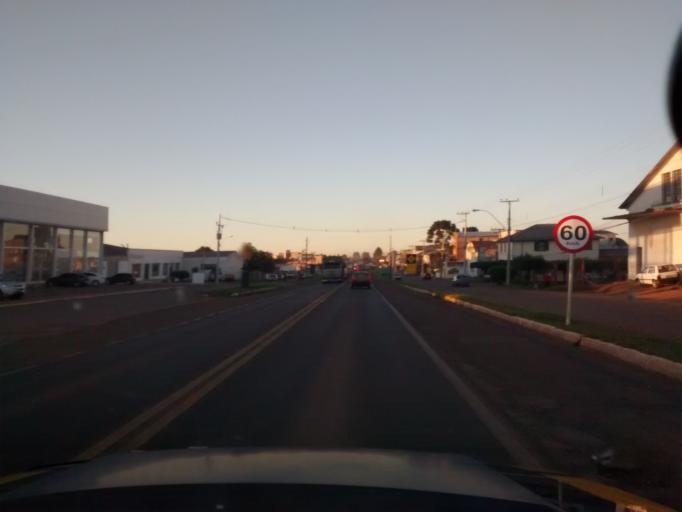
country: BR
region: Rio Grande do Sul
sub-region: Vacaria
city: Vacaria
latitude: -28.5108
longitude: -50.9311
